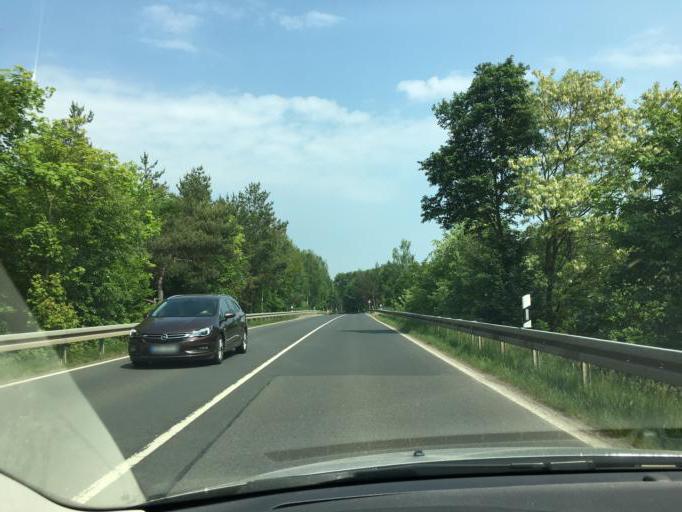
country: DE
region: Saxony
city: Naunhof
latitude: 51.2893
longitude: 12.5872
